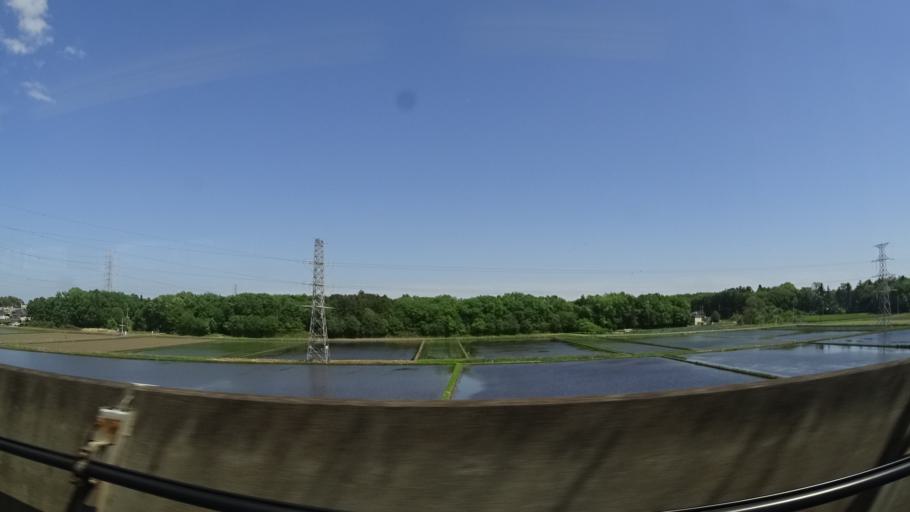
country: JP
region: Tochigi
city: Oyama
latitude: 36.2439
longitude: 139.7644
